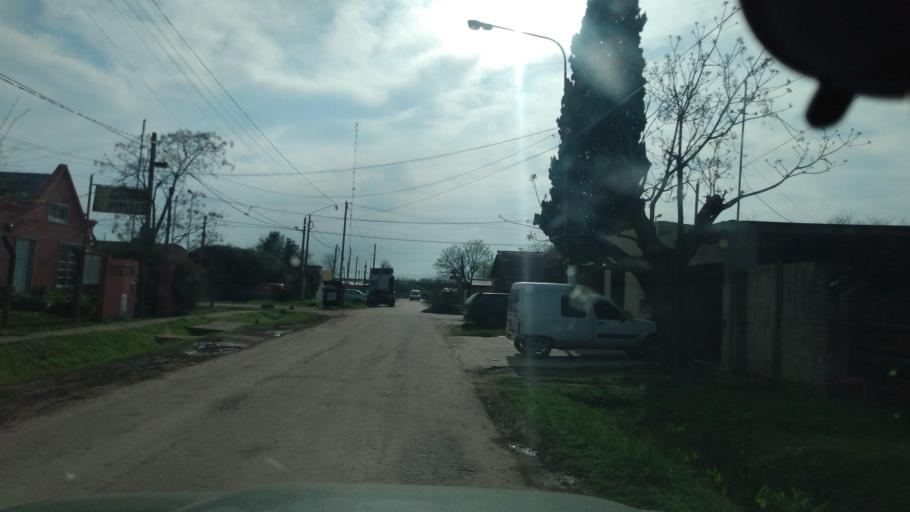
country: AR
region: Buenos Aires
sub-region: Partido de Lujan
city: Lujan
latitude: -34.5504
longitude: -59.1195
